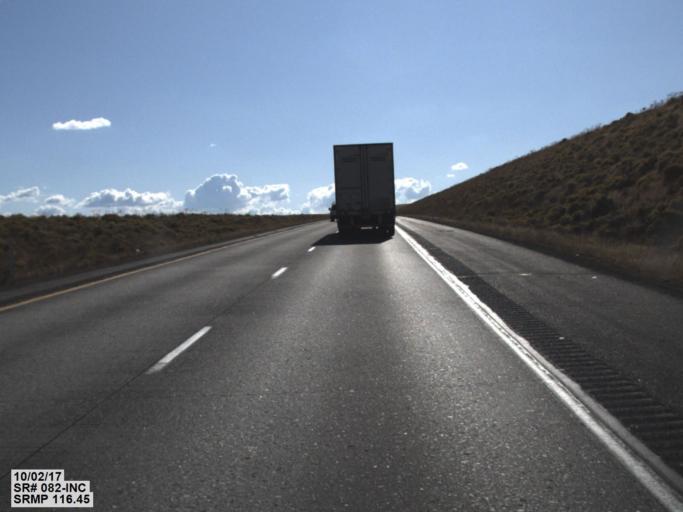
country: US
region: Washington
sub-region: Benton County
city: Highland
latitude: 46.1132
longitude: -119.2058
